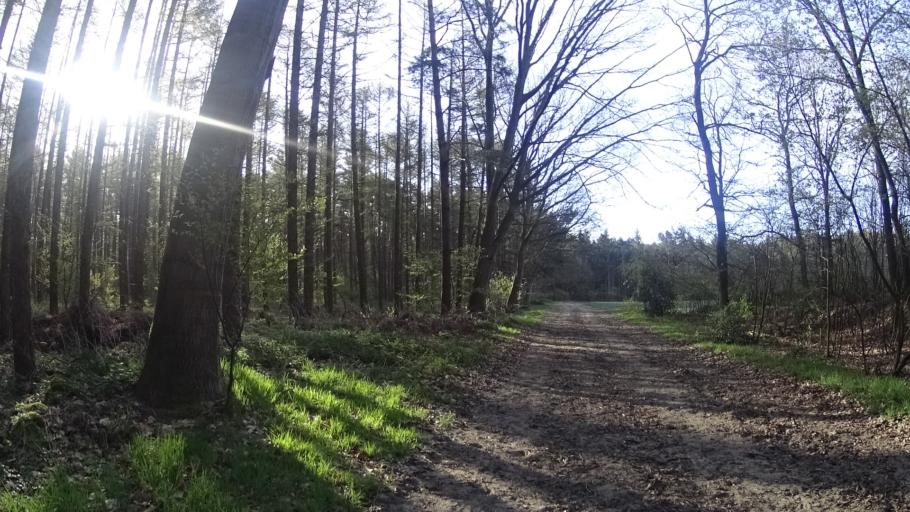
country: DE
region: Lower Saxony
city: Oberlangen
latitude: 52.8153
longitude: 7.2704
